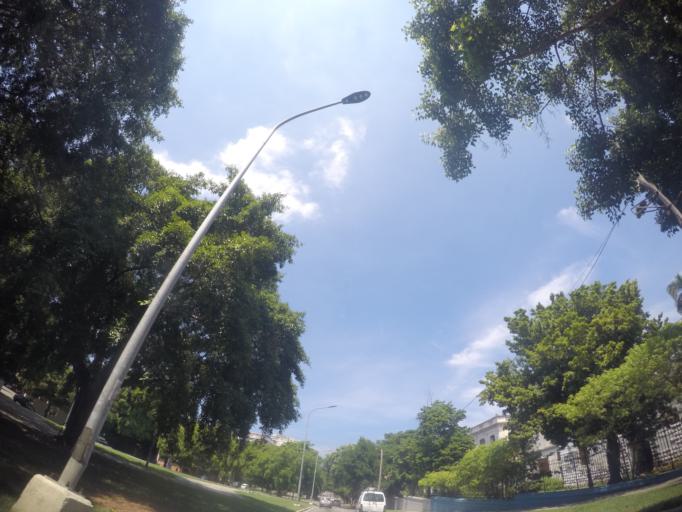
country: CU
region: La Habana
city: Havana
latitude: 23.1358
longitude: -82.3982
